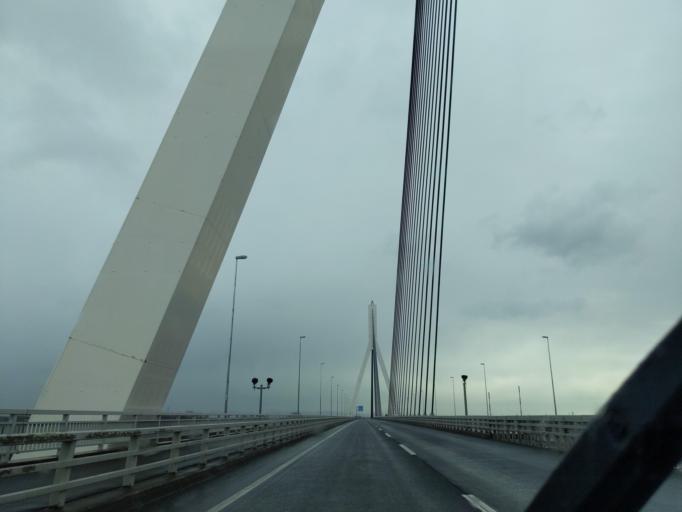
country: JP
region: Hokkaido
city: Ebetsu
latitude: 43.1213
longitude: 141.5800
